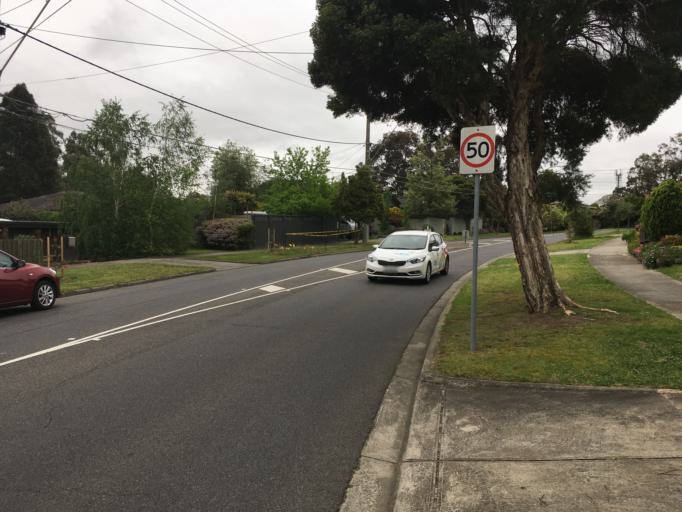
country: AU
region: Victoria
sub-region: Banyule
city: Yallambie
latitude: -37.7282
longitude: 145.1019
